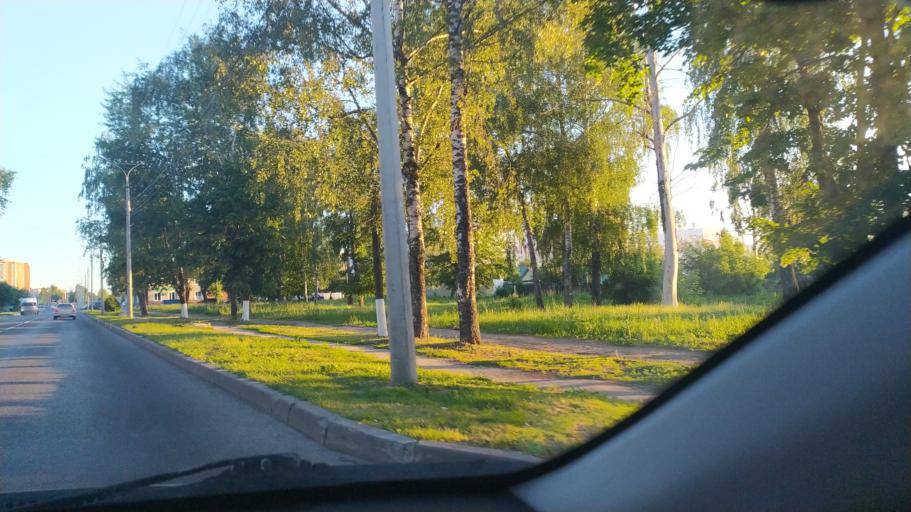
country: RU
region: Chuvashia
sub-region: Cheboksarskiy Rayon
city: Cheboksary
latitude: 56.1200
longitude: 47.2254
